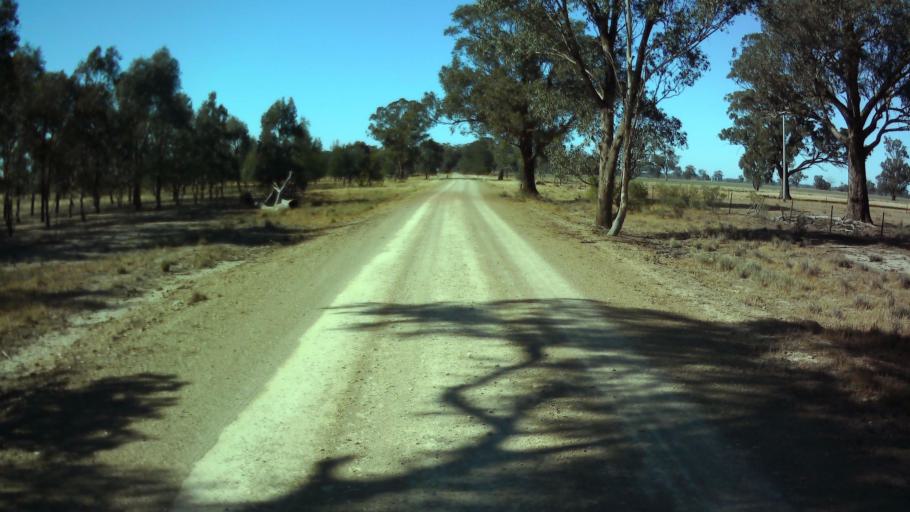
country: AU
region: New South Wales
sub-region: Weddin
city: Grenfell
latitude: -33.9310
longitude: 147.8729
